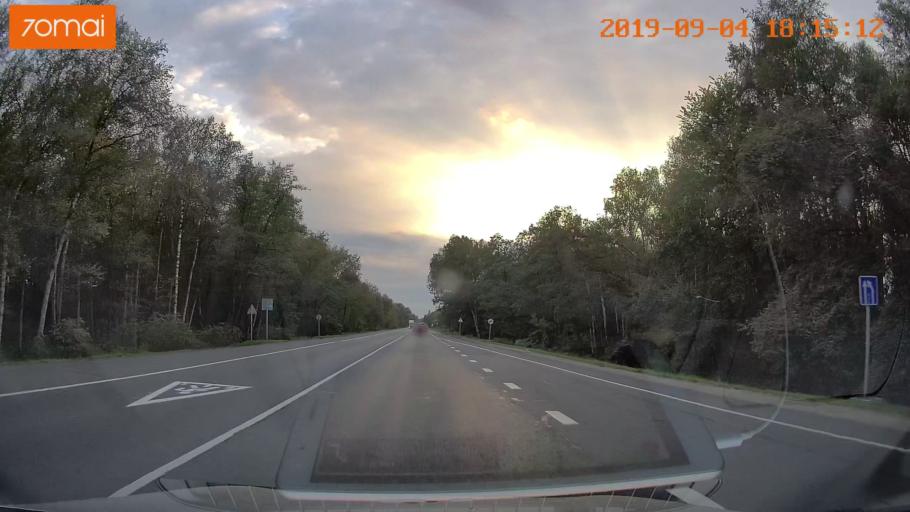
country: RU
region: Moskovskaya
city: Lopatinskiy
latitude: 55.3483
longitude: 38.7075
